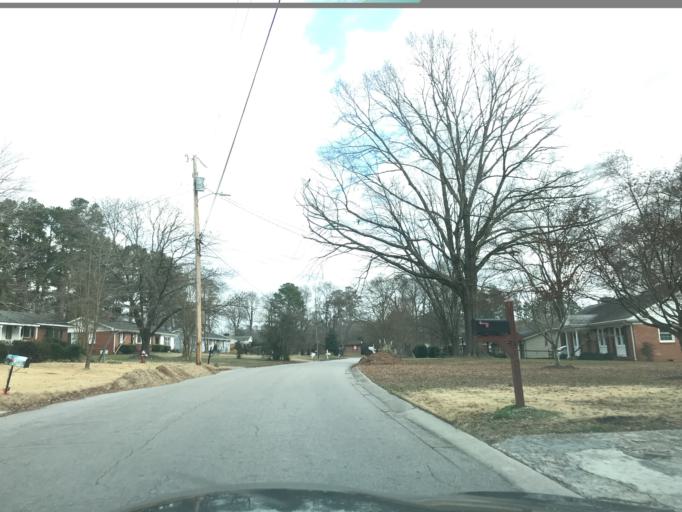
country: US
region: North Carolina
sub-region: Wake County
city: Raleigh
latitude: 35.8237
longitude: -78.5801
